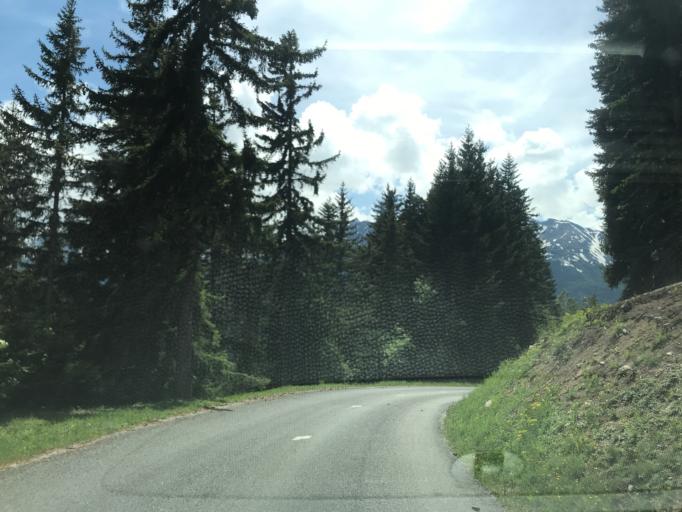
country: FR
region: Rhone-Alpes
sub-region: Departement de la Savoie
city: Modane
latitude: 45.2146
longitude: 6.6484
